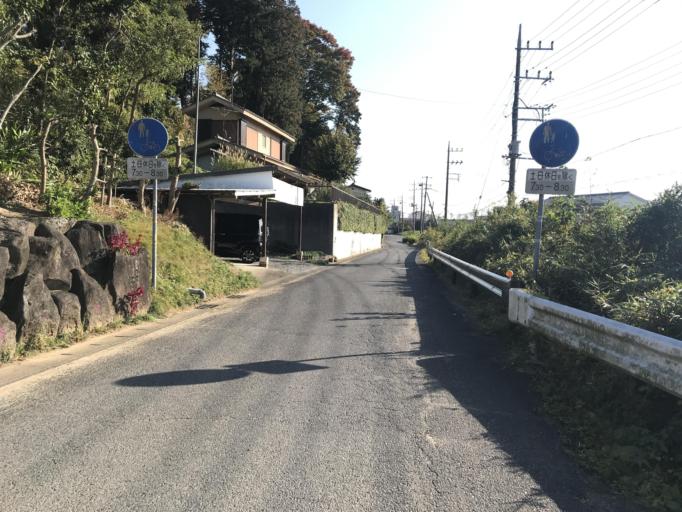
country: JP
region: Ibaraki
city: Ishioka
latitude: 36.1851
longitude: 140.2699
